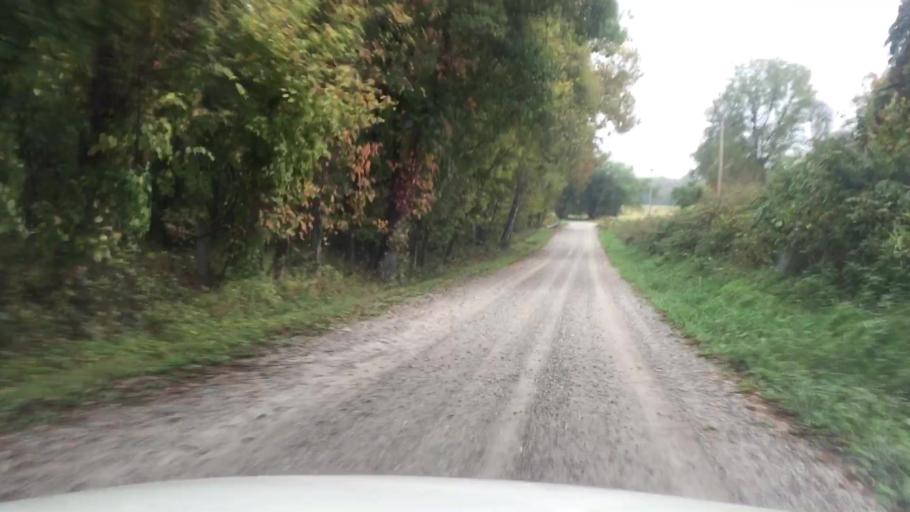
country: US
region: Missouri
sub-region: Boone County
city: Ashland
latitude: 38.8206
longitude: -92.3443
